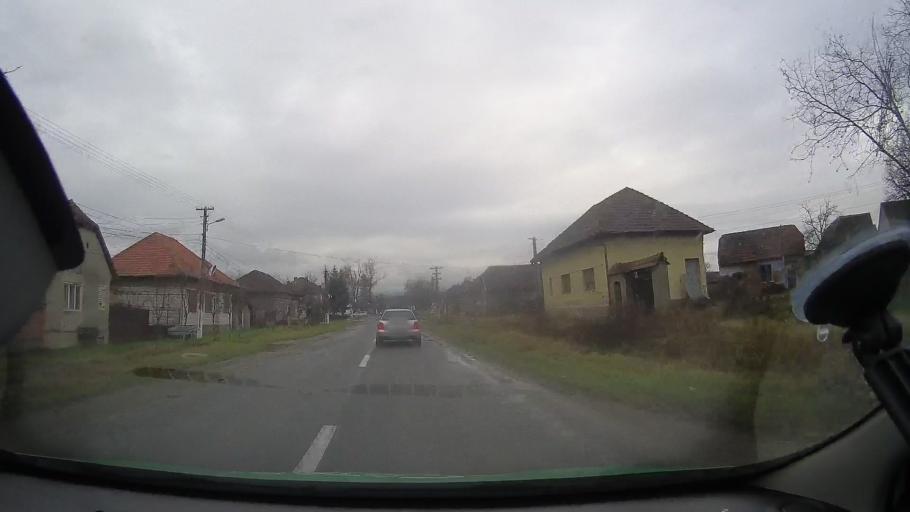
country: RO
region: Arad
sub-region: Comuna Buteni
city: Buteni
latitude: 46.3310
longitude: 22.1252
